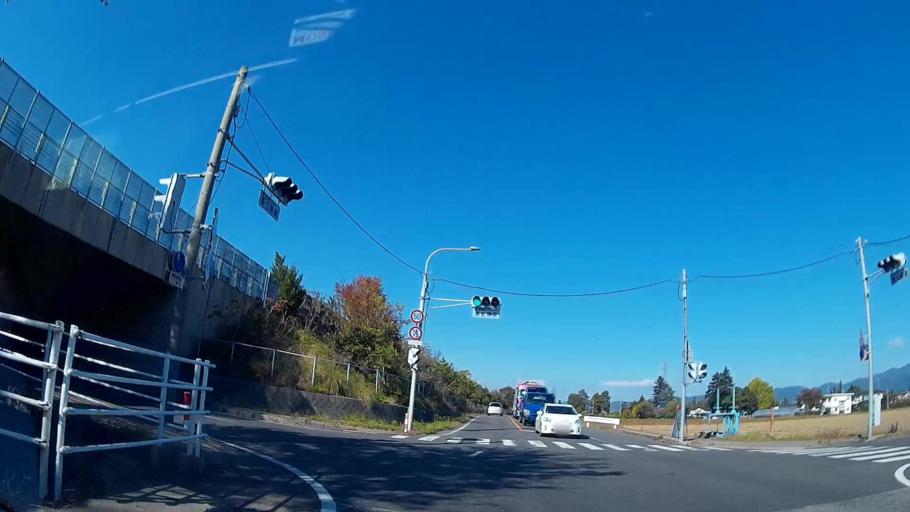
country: JP
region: Nagano
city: Matsumoto
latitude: 36.2079
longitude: 137.9300
